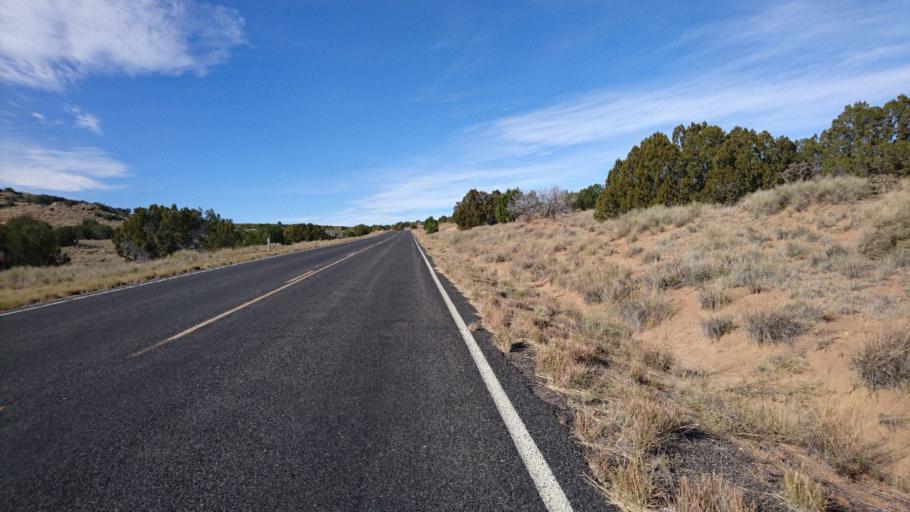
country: US
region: New Mexico
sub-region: Cibola County
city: Laguna
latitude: 35.0414
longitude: -107.3574
